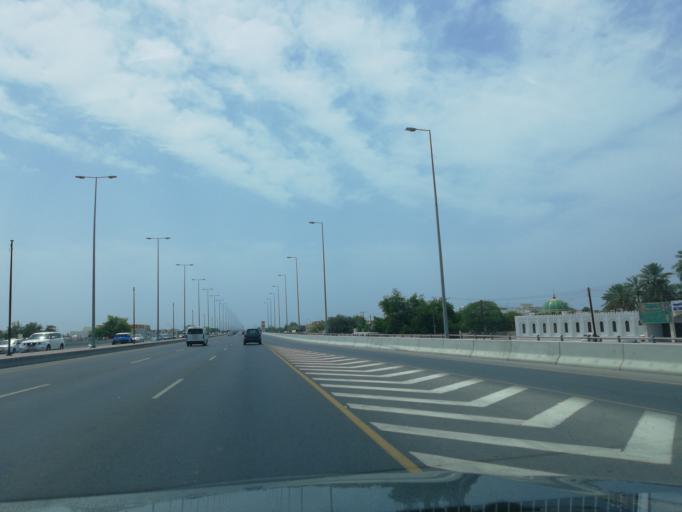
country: OM
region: Muhafazat Masqat
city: As Sib al Jadidah
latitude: 23.6701
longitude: 58.1493
